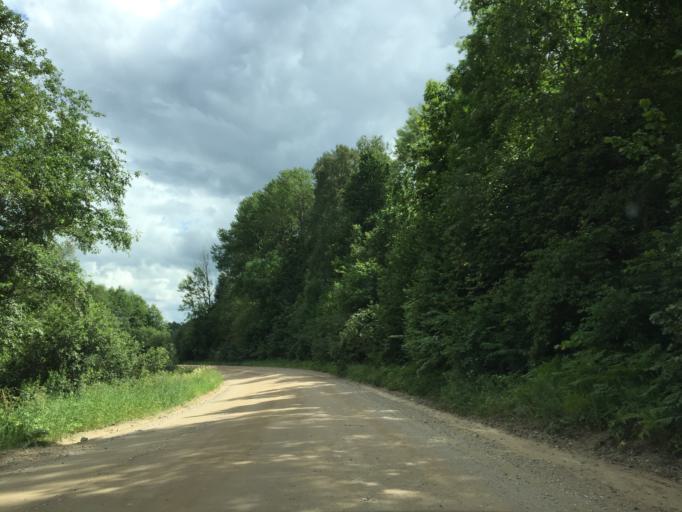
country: LV
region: Ropazu
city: Ropazi
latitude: 56.9094
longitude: 24.7660
